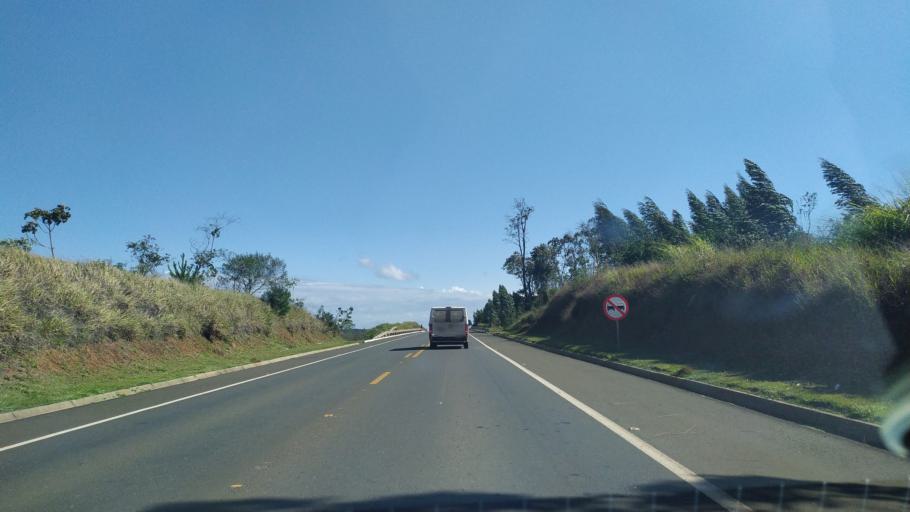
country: BR
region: Parana
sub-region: Ortigueira
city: Ortigueira
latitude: -24.2565
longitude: -50.7830
